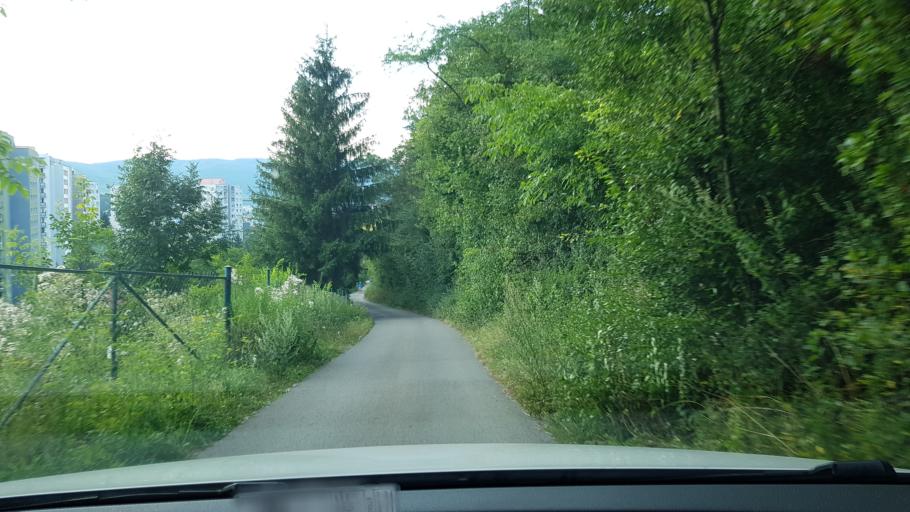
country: SK
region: Trenciansky
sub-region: Okres Povazska Bystrica
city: Povazska Bystrica
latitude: 49.1124
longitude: 18.4552
